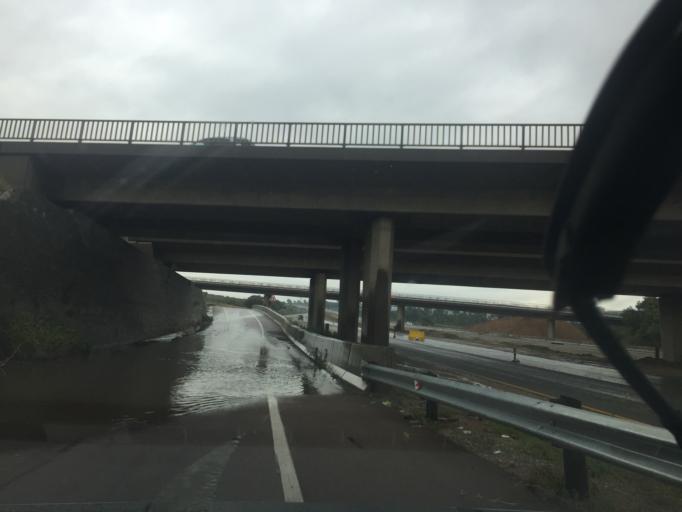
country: ZA
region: Gauteng
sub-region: City of Tshwane Metropolitan Municipality
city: Centurion
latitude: -25.8936
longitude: 28.1046
